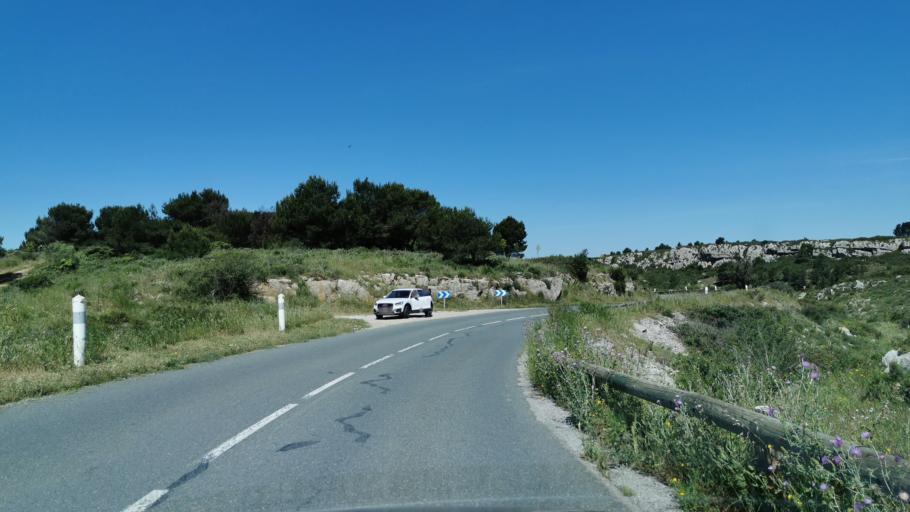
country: FR
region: Languedoc-Roussillon
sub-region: Departement de l'Aude
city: Armissan
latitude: 43.1766
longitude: 3.1025
